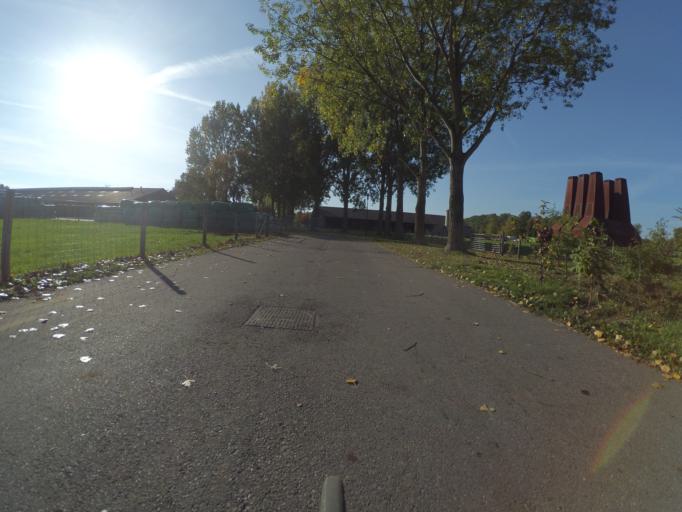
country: NL
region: Utrecht
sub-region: Gemeente Bunnik
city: Bunnik
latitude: 52.0825
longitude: 5.1860
